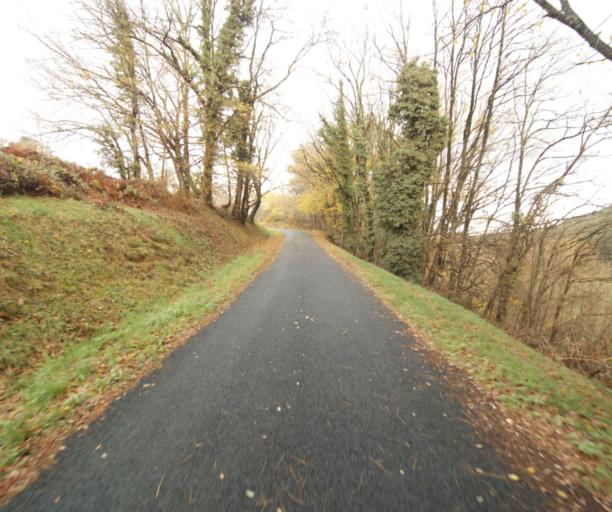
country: FR
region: Limousin
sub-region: Departement de la Correze
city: Cornil
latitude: 45.2033
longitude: 1.6584
